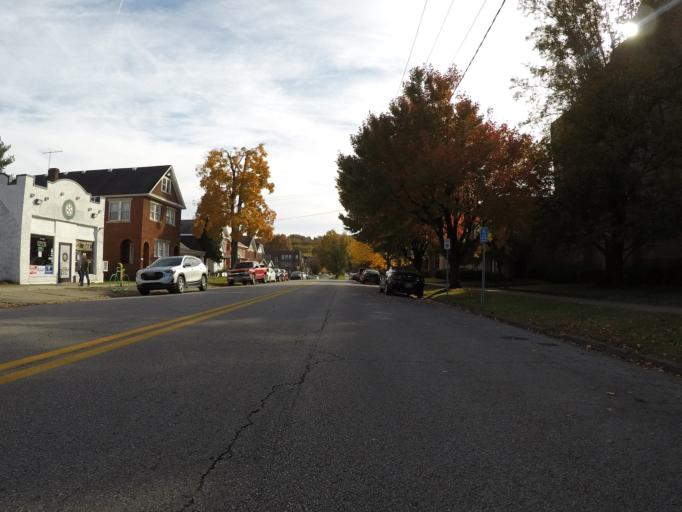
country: US
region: West Virginia
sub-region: Cabell County
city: Huntington
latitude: 38.4125
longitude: -82.4398
